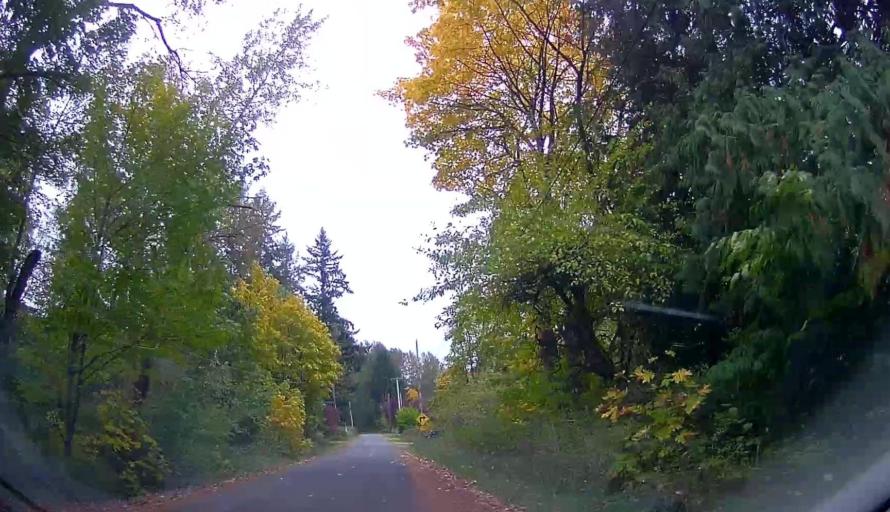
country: US
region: Washington
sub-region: Skagit County
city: Sedro-Woolley
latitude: 48.5240
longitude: -122.0882
